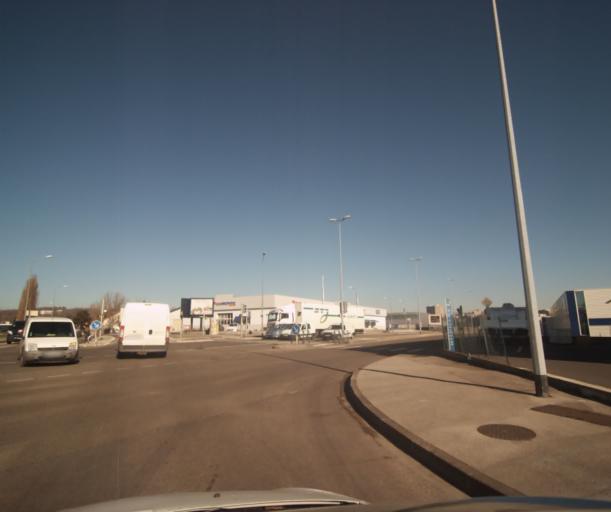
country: FR
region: Franche-Comte
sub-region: Departement du Doubs
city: Besancon
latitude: 47.2381
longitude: 5.9882
